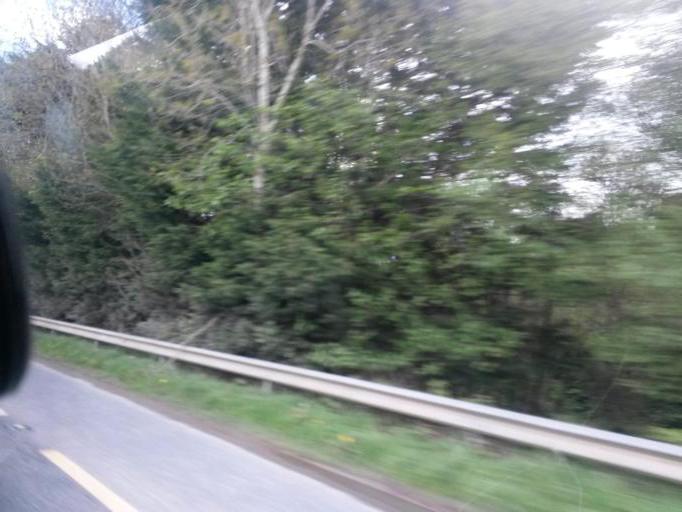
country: IE
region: Leinster
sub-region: Loch Garman
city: Enniscorthy
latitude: 52.4760
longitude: -6.5627
